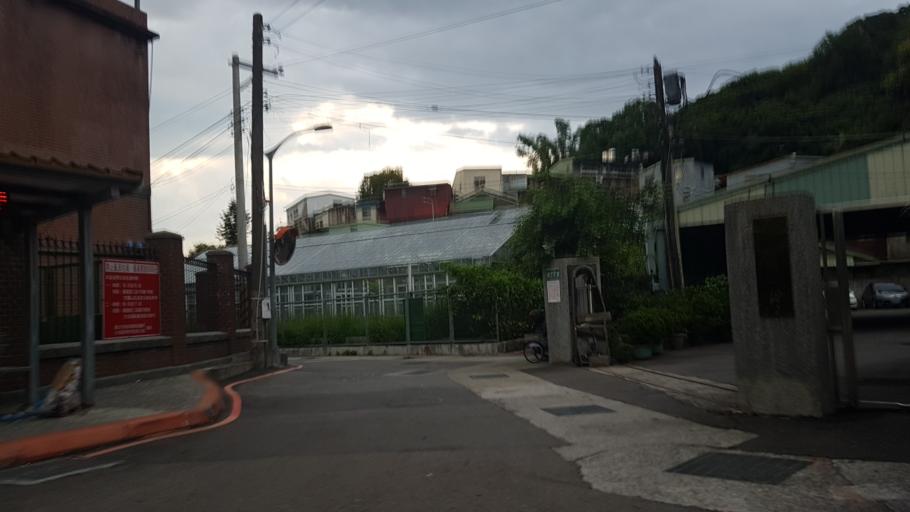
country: TW
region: Taipei
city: Taipei
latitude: 25.0124
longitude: 121.5479
